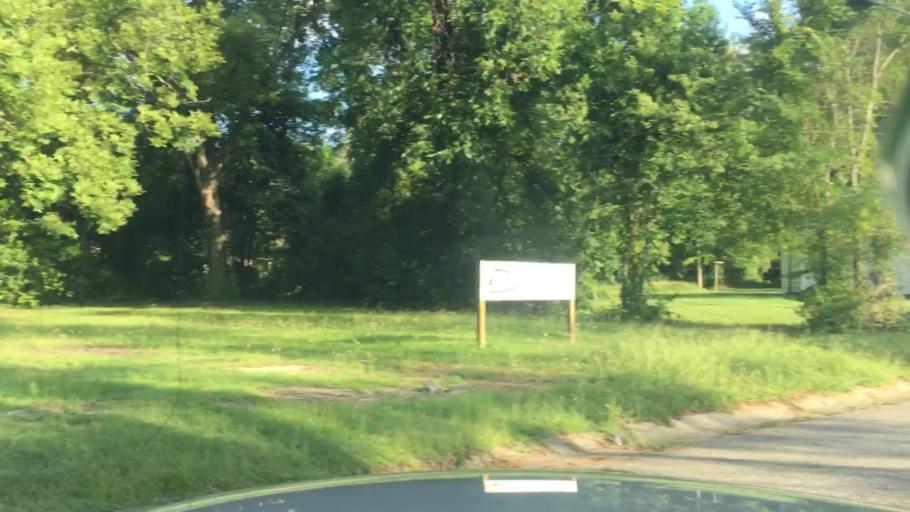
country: US
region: North Carolina
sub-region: Cumberland County
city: Fayetteville
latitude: 35.0500
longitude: -78.8907
